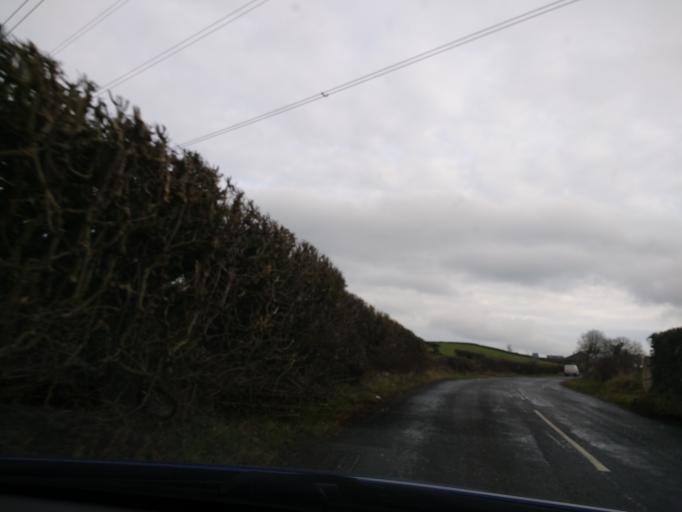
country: GB
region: England
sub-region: Lancashire
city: Caton
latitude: 54.0837
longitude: -2.7497
